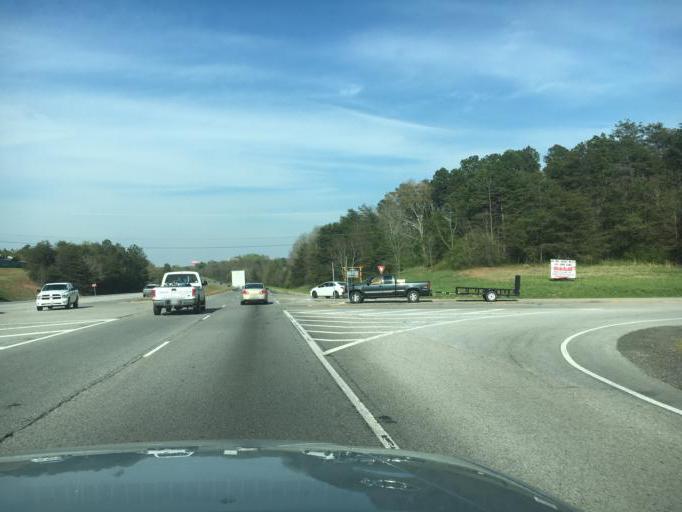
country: US
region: Georgia
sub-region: Habersham County
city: Raoul
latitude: 34.4492
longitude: -83.6182
